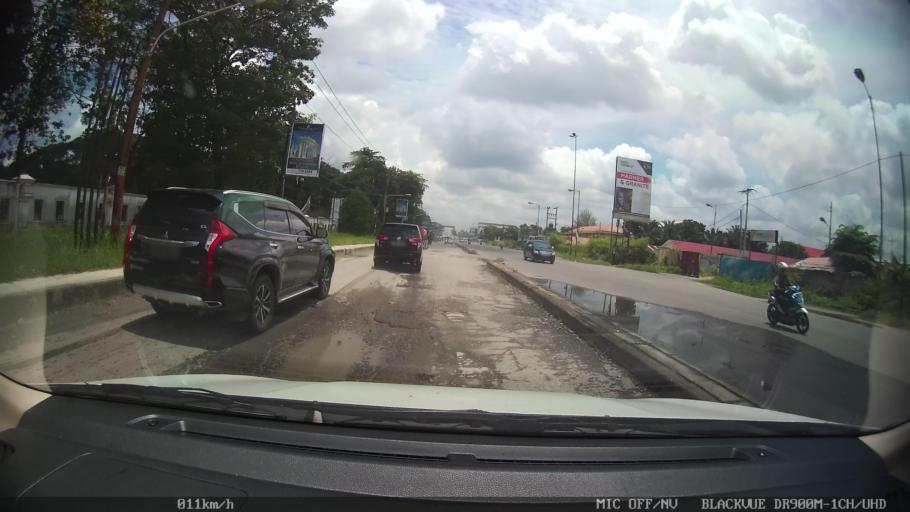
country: ID
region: North Sumatra
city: Medan
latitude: 3.6059
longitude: 98.7152
